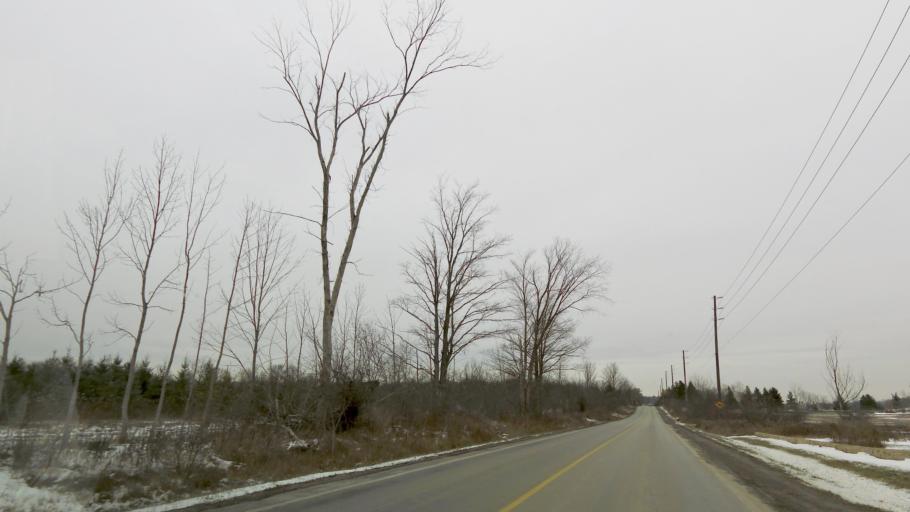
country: CA
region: Ontario
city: Vaughan
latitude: 43.8722
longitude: -79.6125
